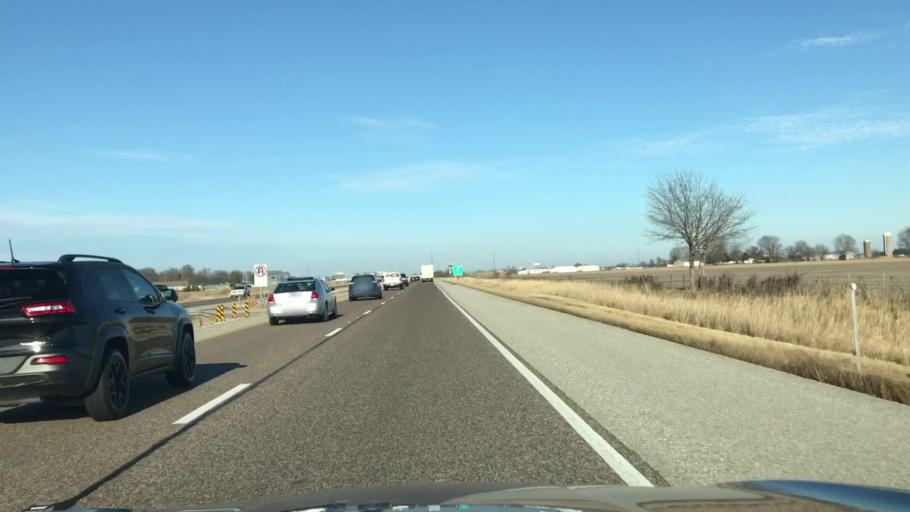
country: US
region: Illinois
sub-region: Madison County
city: Worden
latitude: 38.8775
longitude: -89.8460
